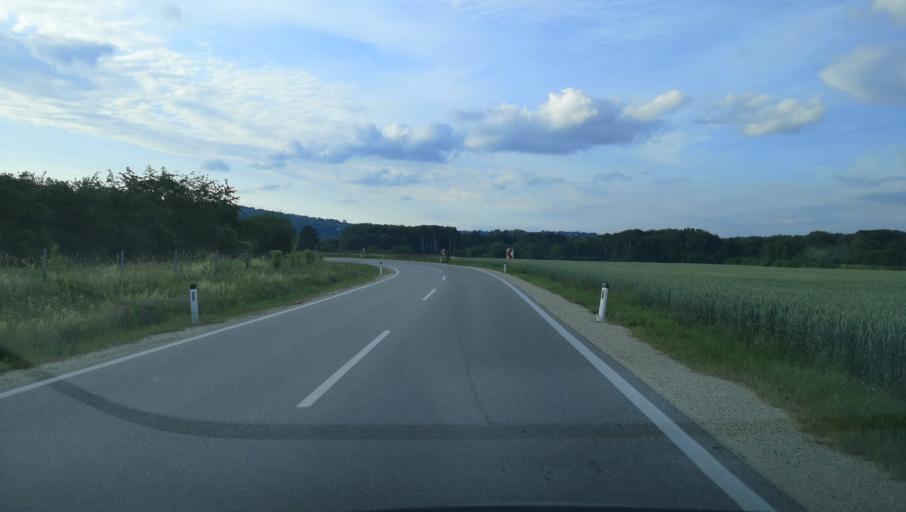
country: AT
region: Lower Austria
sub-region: Politischer Bezirk Krems
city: Weinzierl bei Krems
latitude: 48.3918
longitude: 15.5984
